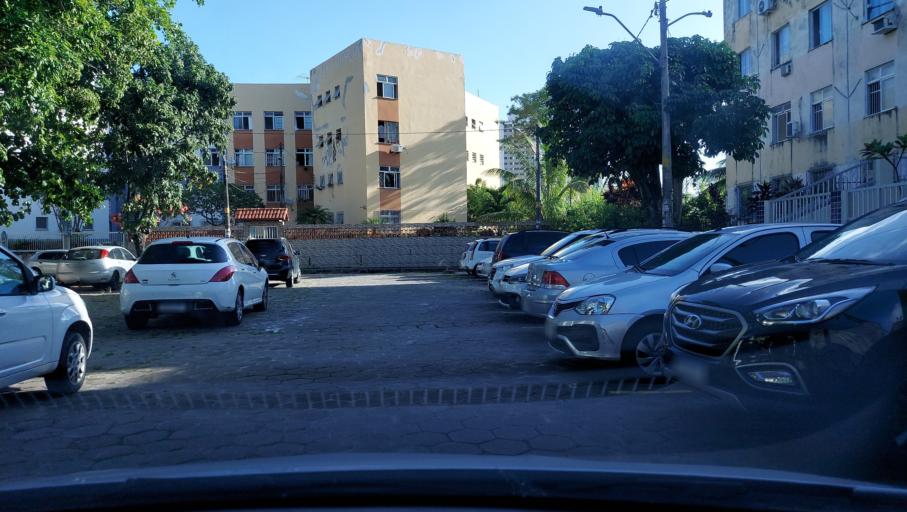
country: BR
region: Bahia
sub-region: Salvador
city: Salvador
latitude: -12.9778
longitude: -38.4466
